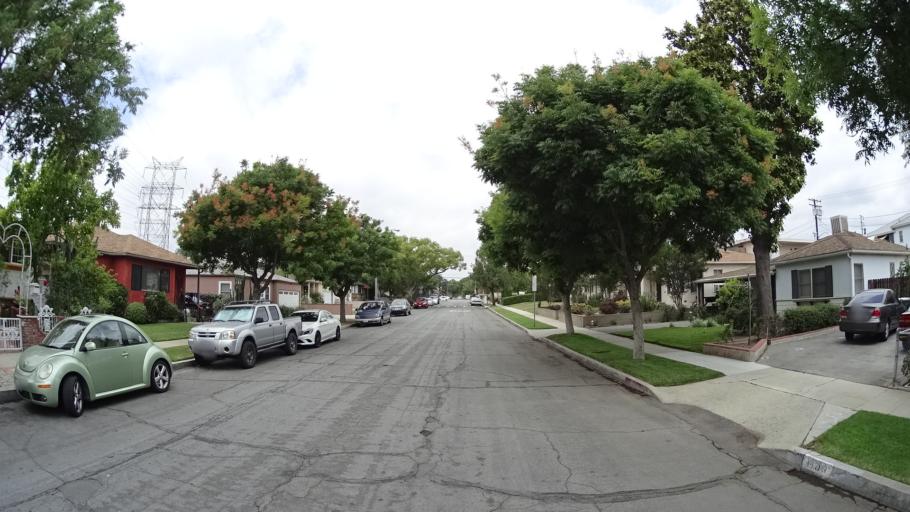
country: US
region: California
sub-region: Los Angeles County
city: Universal City
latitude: 34.1661
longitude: -118.3473
